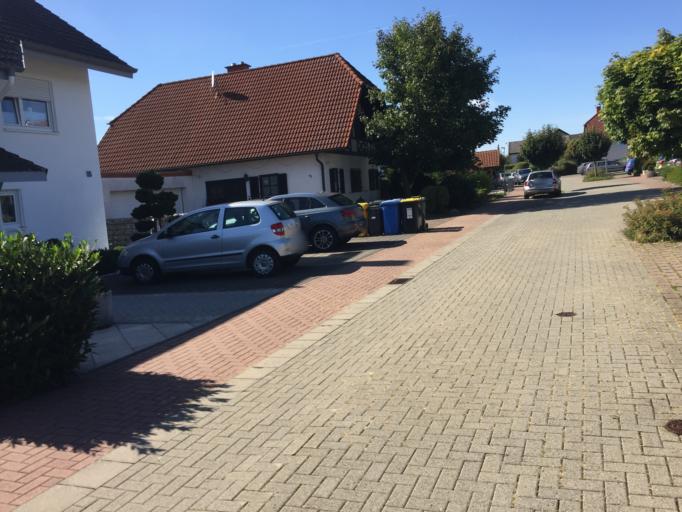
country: DE
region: Hesse
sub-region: Regierungsbezirk Giessen
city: Reiskirchen
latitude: 50.5950
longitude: 8.8568
